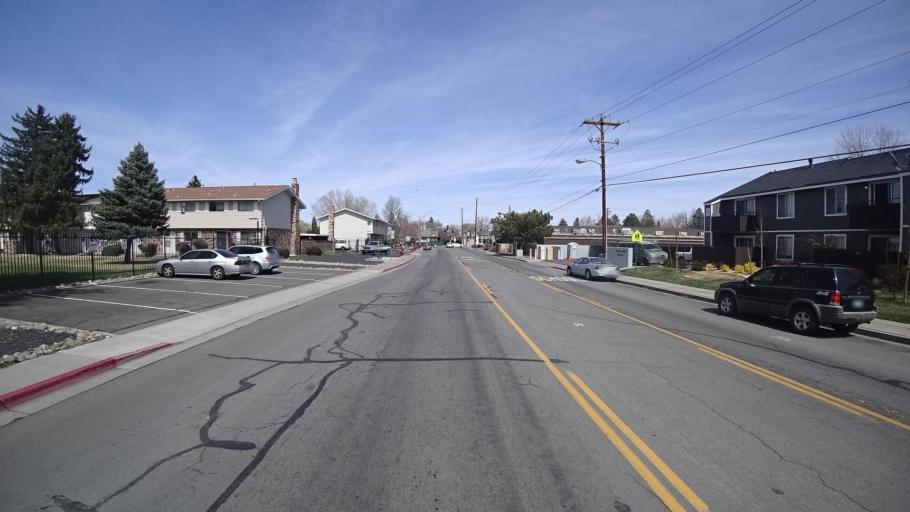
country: US
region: Nevada
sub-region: Washoe County
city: Reno
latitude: 39.4828
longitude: -119.7808
